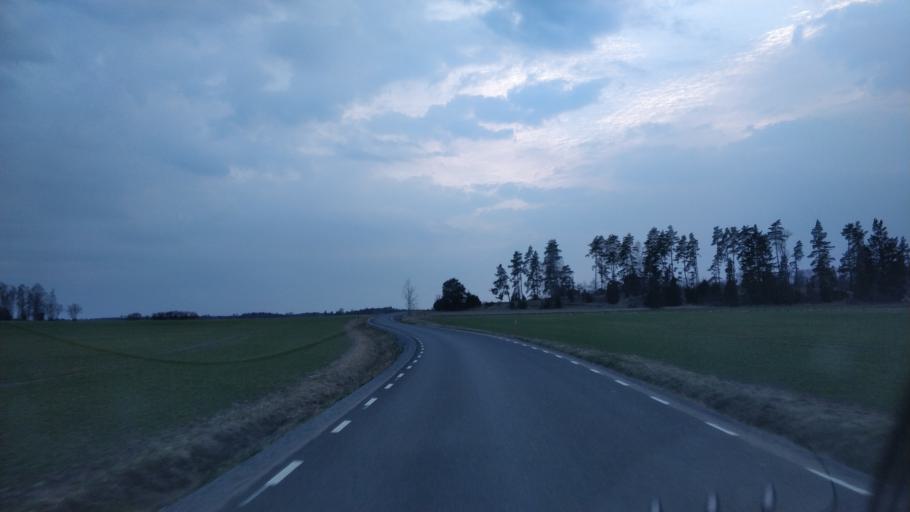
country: SE
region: Uppsala
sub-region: Enkopings Kommun
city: Orsundsbro
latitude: 59.7205
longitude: 17.2651
